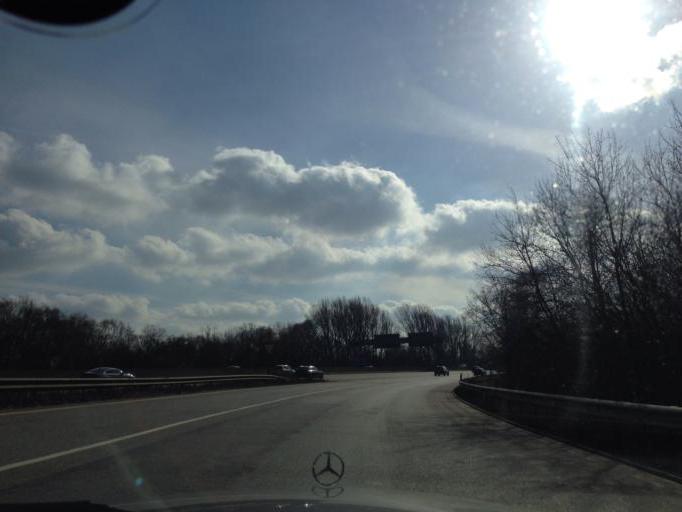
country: DE
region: Hamburg
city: Rothenburgsort
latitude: 53.5021
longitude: 10.0386
